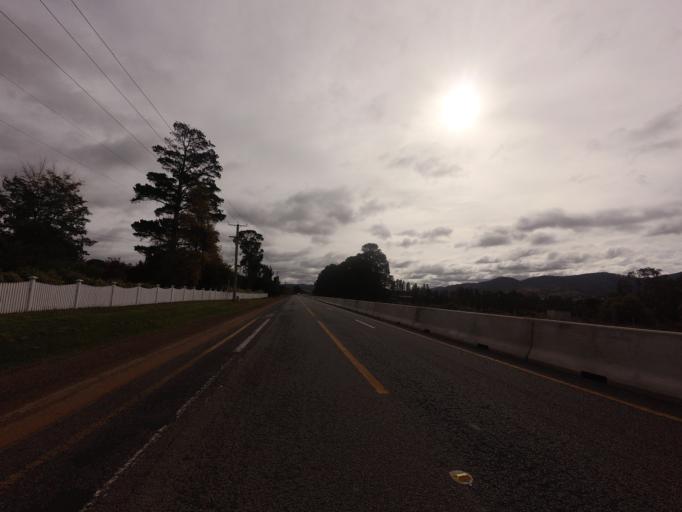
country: AU
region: Tasmania
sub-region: Brighton
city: Bridgewater
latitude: -42.6713
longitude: 147.2571
